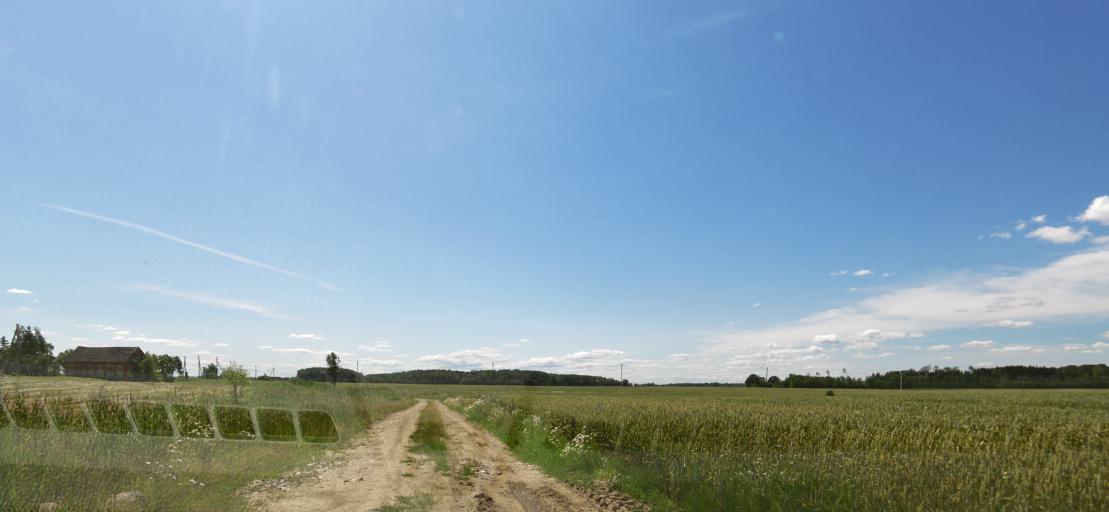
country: LT
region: Panevezys
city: Pasvalys
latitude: 56.2668
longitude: 24.5131
